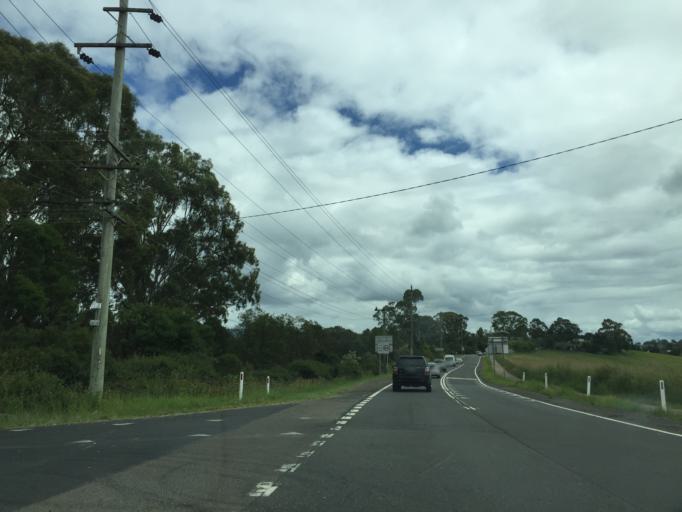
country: AU
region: New South Wales
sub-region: Hawkesbury
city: Richmond
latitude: -33.5694
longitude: 150.7052
